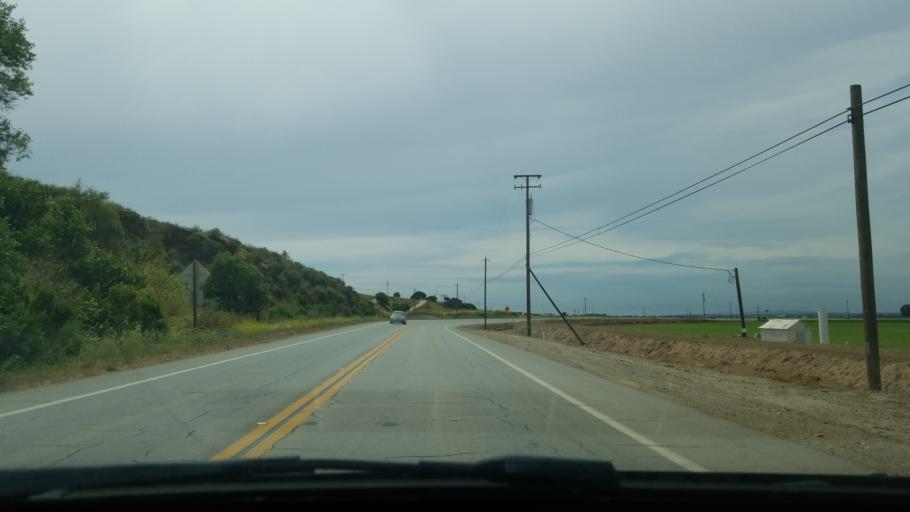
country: US
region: California
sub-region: Santa Barbara County
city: Santa Maria
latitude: 34.9089
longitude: -120.3441
